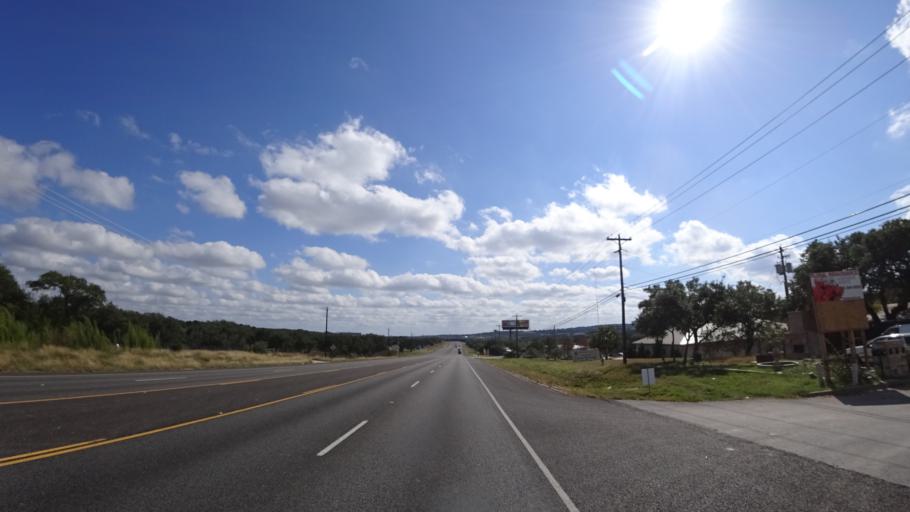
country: US
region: Texas
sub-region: Travis County
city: Barton Creek
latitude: 30.2581
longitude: -97.9055
